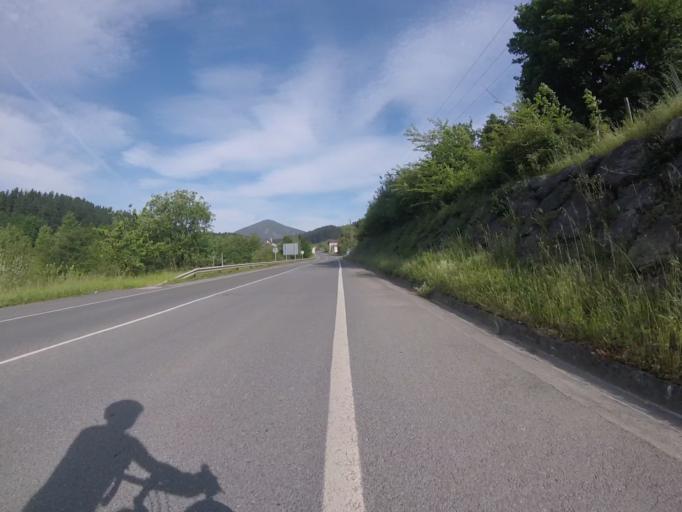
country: ES
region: Basque Country
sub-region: Provincia de Guipuzcoa
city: Zumarraga
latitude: 43.0762
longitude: -2.2913
